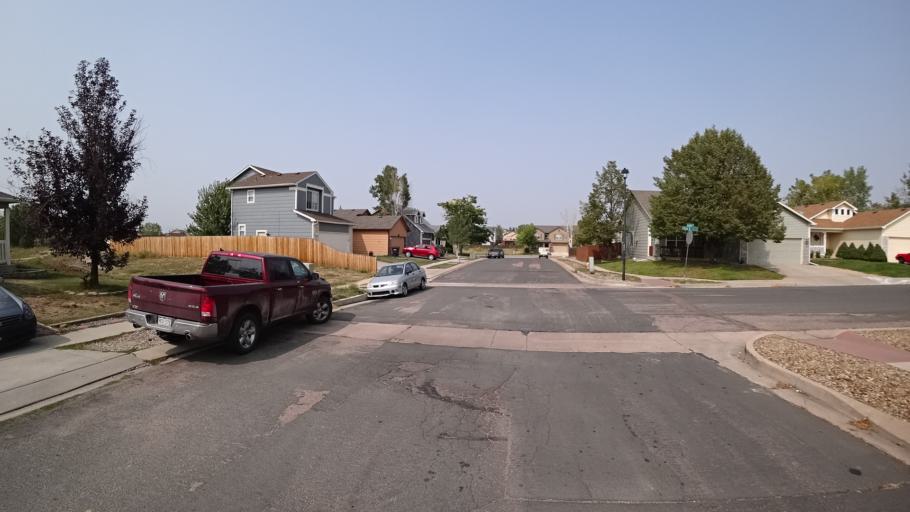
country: US
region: Colorado
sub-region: El Paso County
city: Cimarron Hills
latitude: 38.9232
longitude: -104.7324
